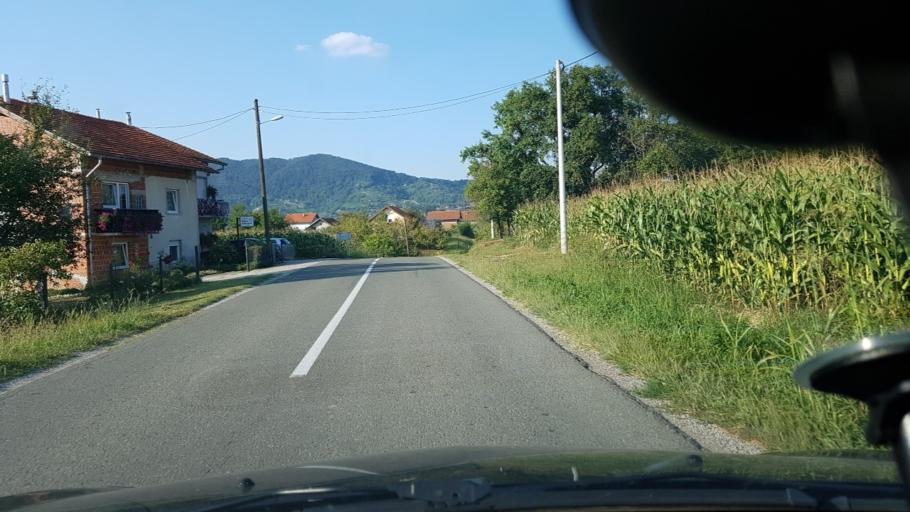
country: SI
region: Bistrica ob Sotli
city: Bistrica ob Sotli
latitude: 46.0284
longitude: 15.7317
